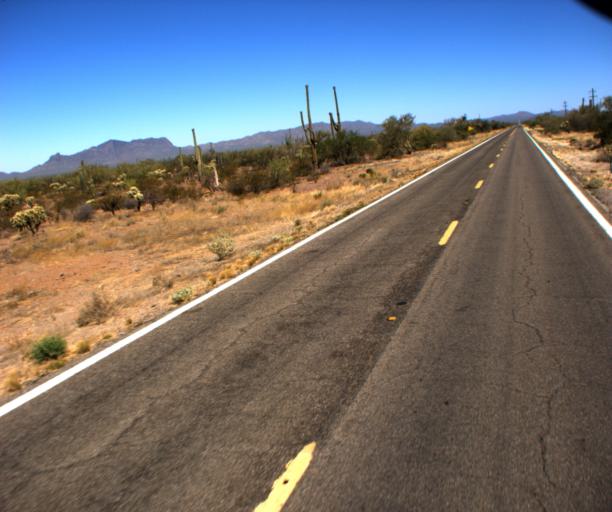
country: US
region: Arizona
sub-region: Pima County
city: Sells
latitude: 32.0201
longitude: -112.0014
